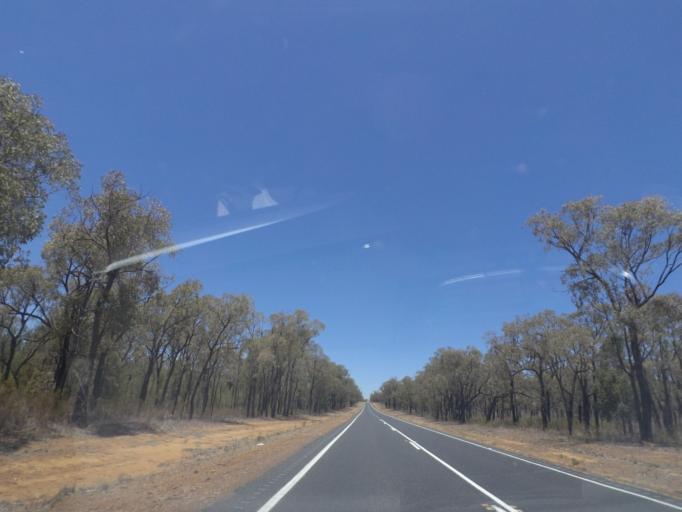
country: AU
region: New South Wales
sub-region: Narrabri
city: Narrabri
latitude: -30.7378
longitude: 149.5171
